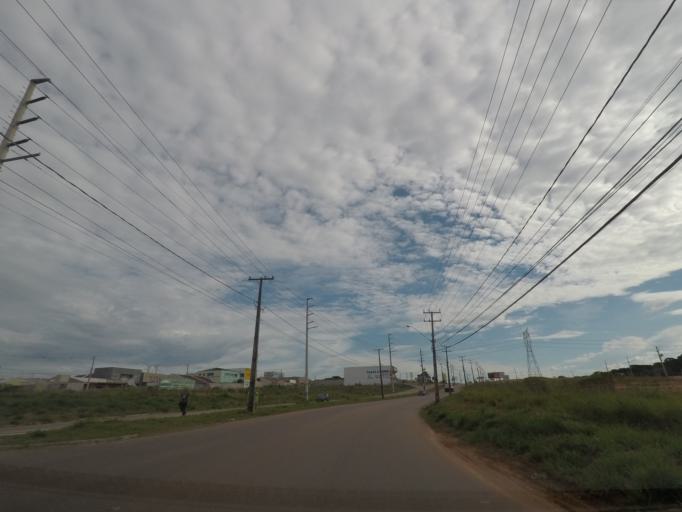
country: BR
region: Parana
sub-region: Araucaria
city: Araucaria
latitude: -25.6347
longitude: -49.2934
